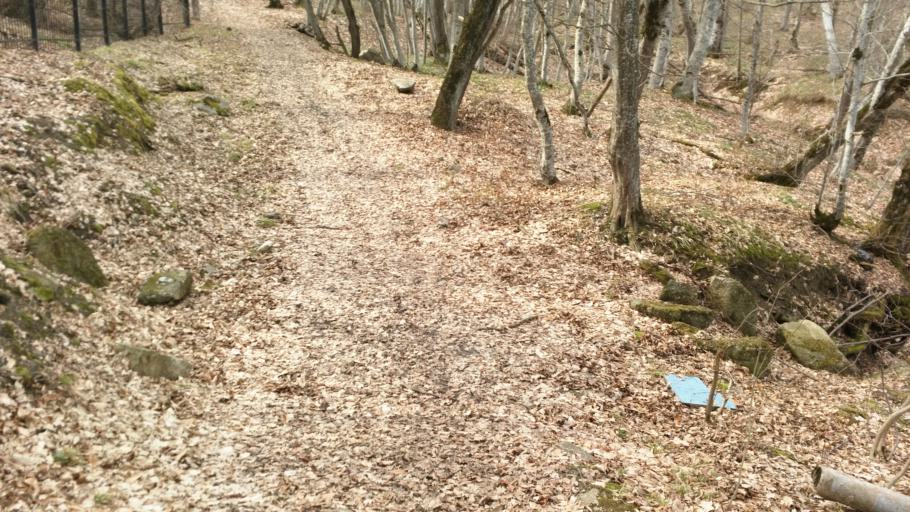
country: RU
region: Stavropol'skiy
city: Zheleznovodsk
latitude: 44.1298
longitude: 43.0247
